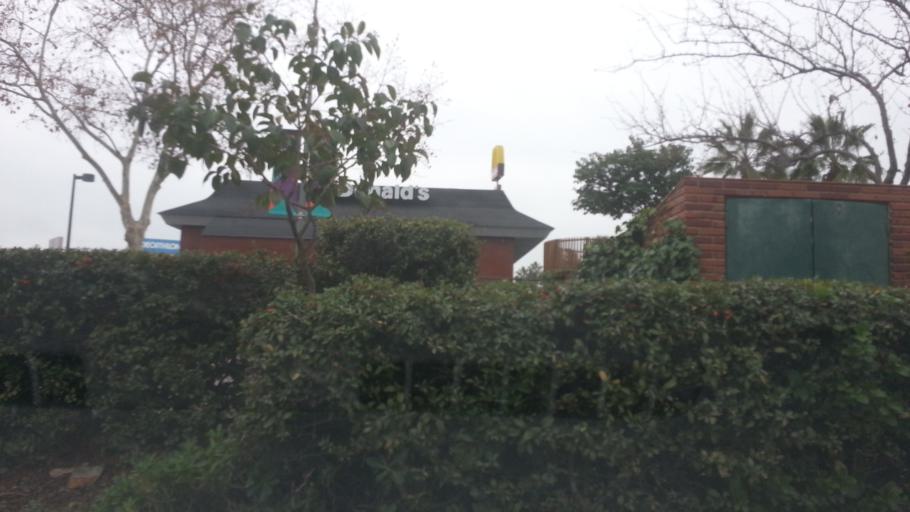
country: ES
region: Catalonia
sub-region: Provincia de Barcelona
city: Terrassa
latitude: 41.5461
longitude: 2.0263
